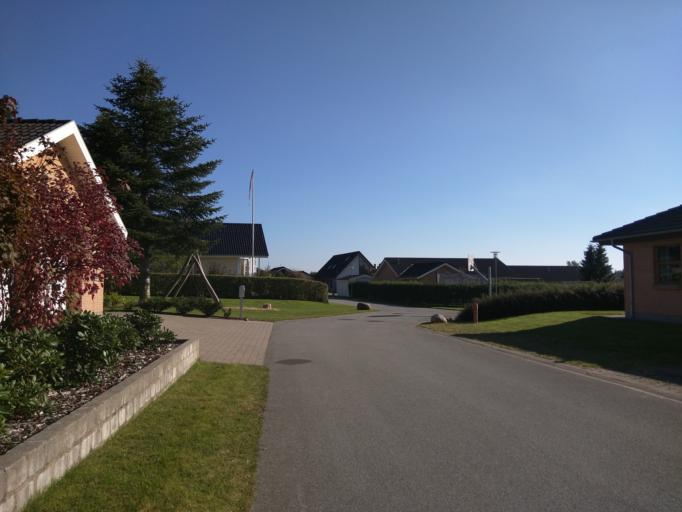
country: DK
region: Central Jutland
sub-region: Viborg Kommune
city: Viborg
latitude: 56.4346
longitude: 9.3810
